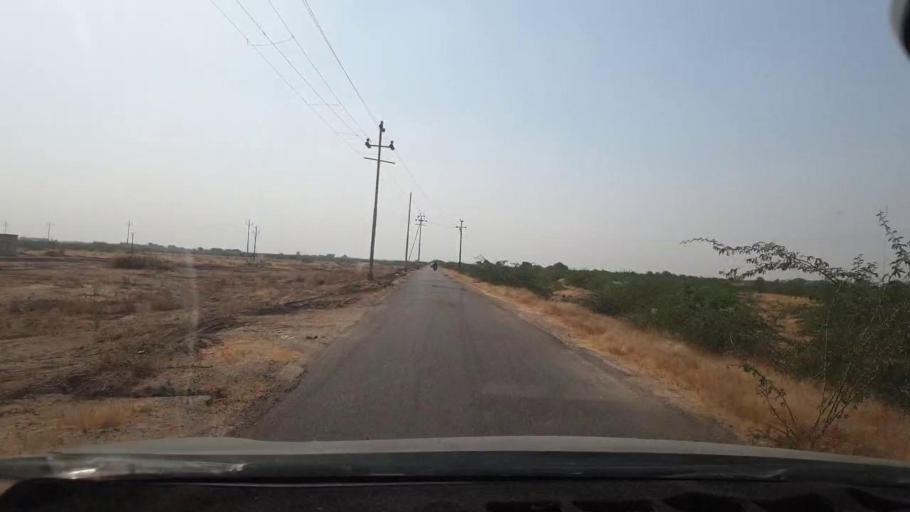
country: PK
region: Sindh
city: Malir Cantonment
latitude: 25.1083
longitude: 67.2024
